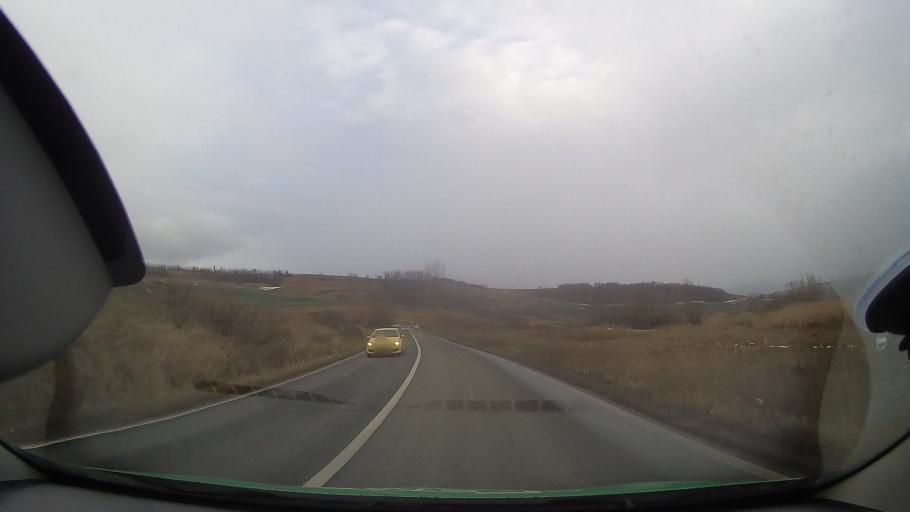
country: RO
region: Sibiu
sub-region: Comuna Blajel
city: Blajel
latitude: 46.2289
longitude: 24.3116
